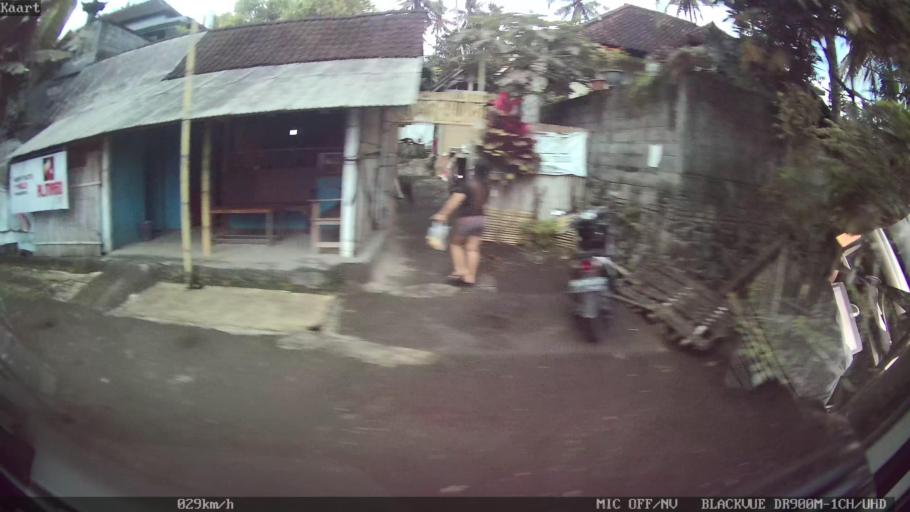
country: ID
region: Bali
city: Banjar Parekan
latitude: -8.5708
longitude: 115.2034
